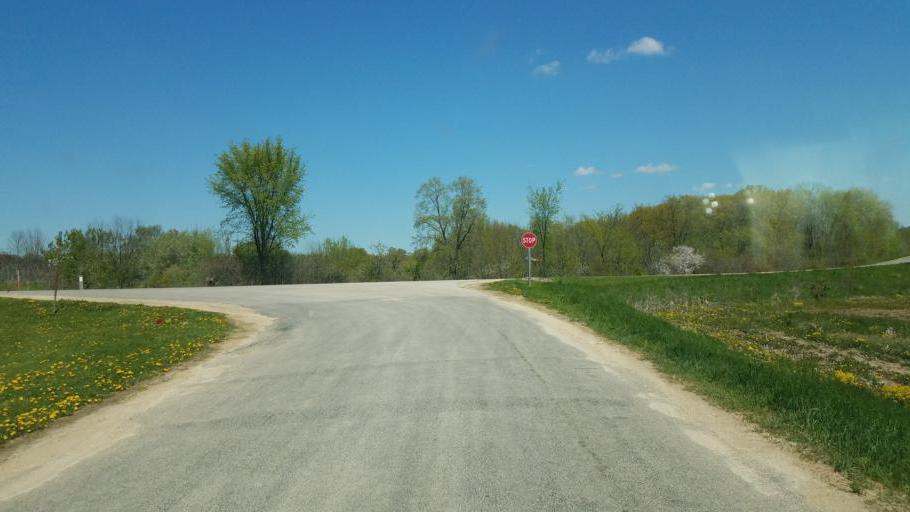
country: US
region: Wisconsin
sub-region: Vernon County
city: Hillsboro
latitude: 43.5994
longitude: -90.4719
